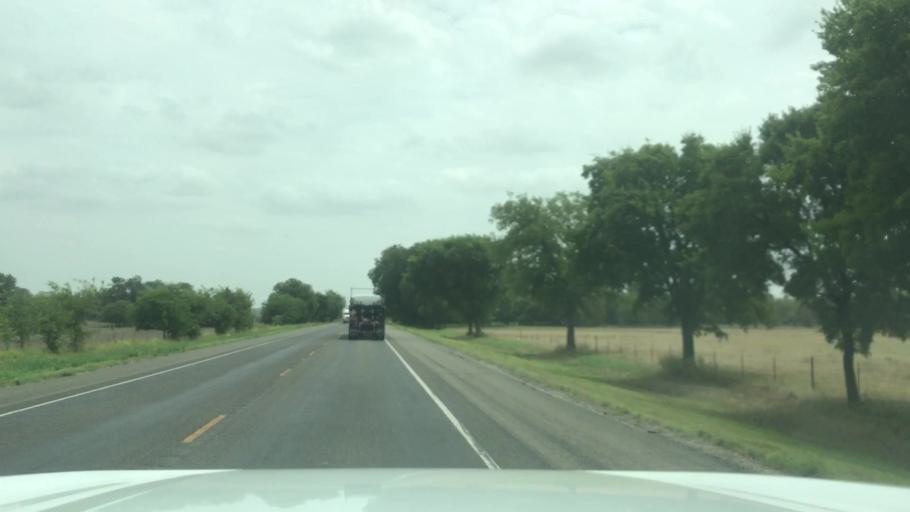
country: US
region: Texas
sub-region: Bosque County
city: Valley Mills
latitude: 31.6719
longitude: -97.5048
